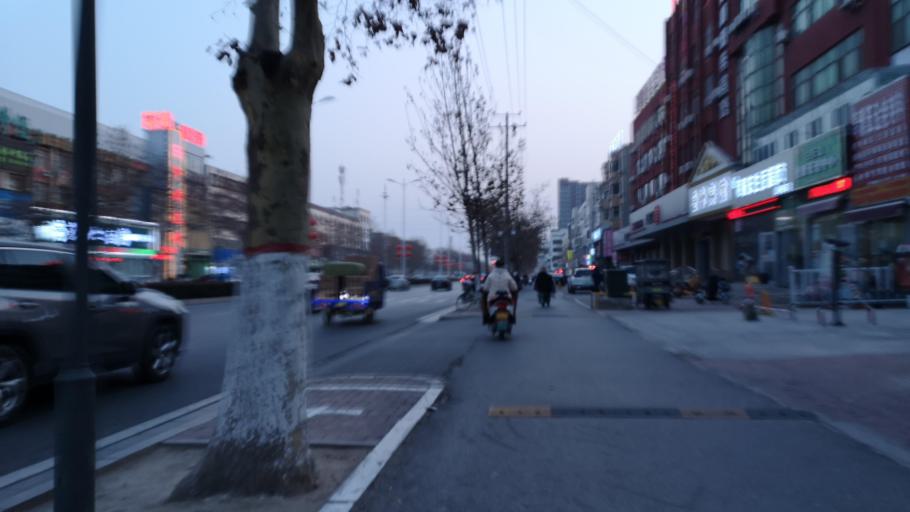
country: CN
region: Henan Sheng
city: Zhongyuanlu
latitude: 35.7677
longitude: 115.0687
